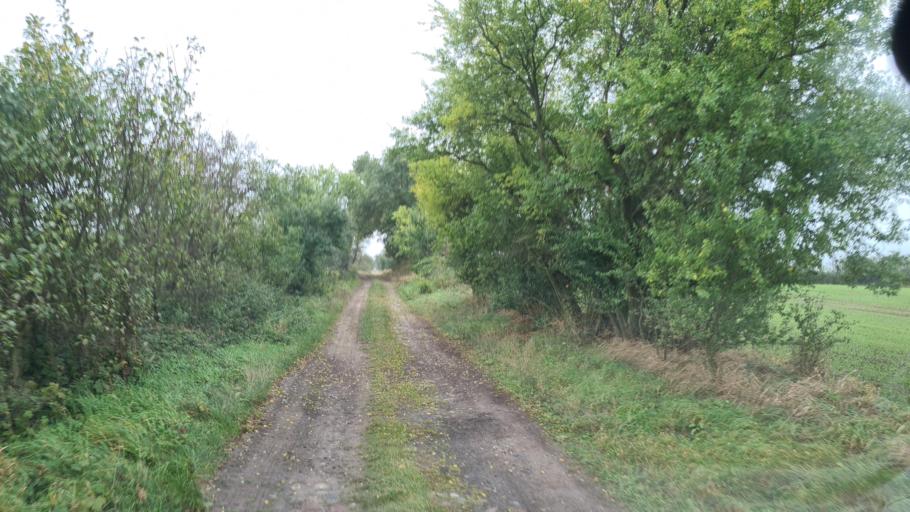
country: DE
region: Brandenburg
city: Furstenwalde
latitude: 52.4130
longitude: 14.0328
